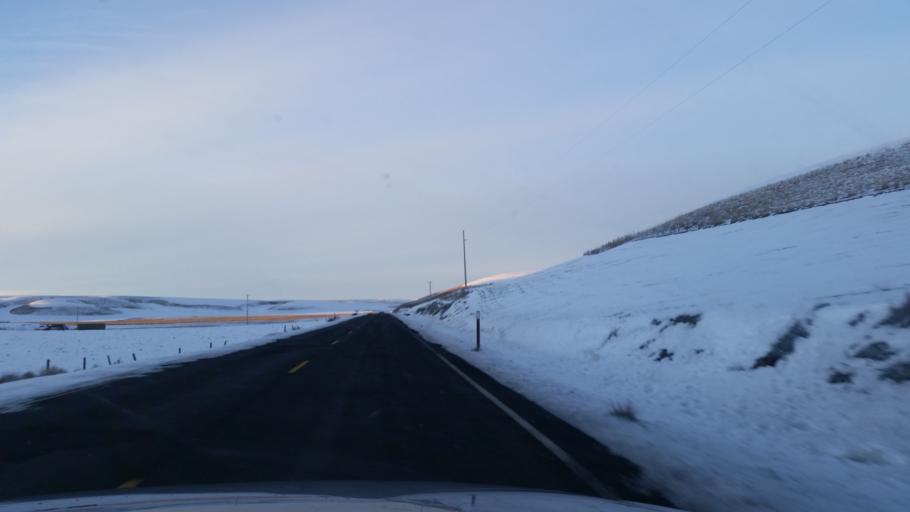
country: US
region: Washington
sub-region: Spokane County
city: Cheney
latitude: 47.1167
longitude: -117.8239
